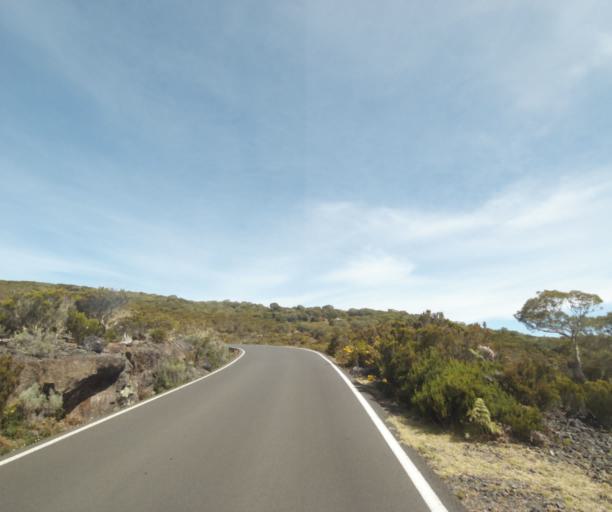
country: RE
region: Reunion
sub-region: Reunion
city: Trois-Bassins
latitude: -21.0693
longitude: 55.3788
